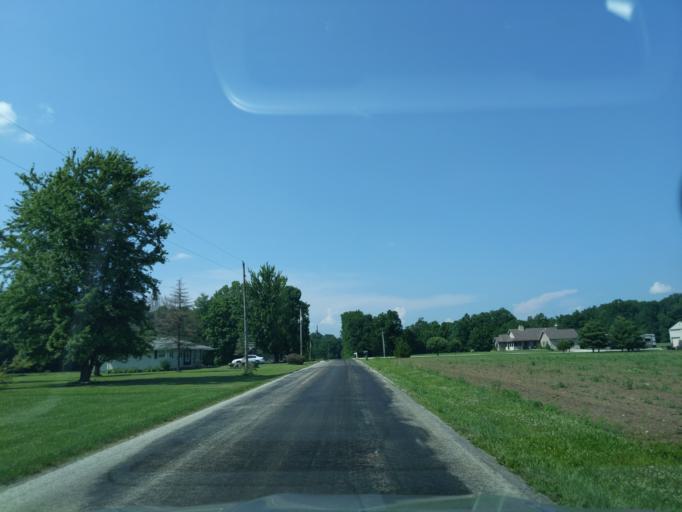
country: US
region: Indiana
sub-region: Ripley County
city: Osgood
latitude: 39.1211
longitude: -85.3422
